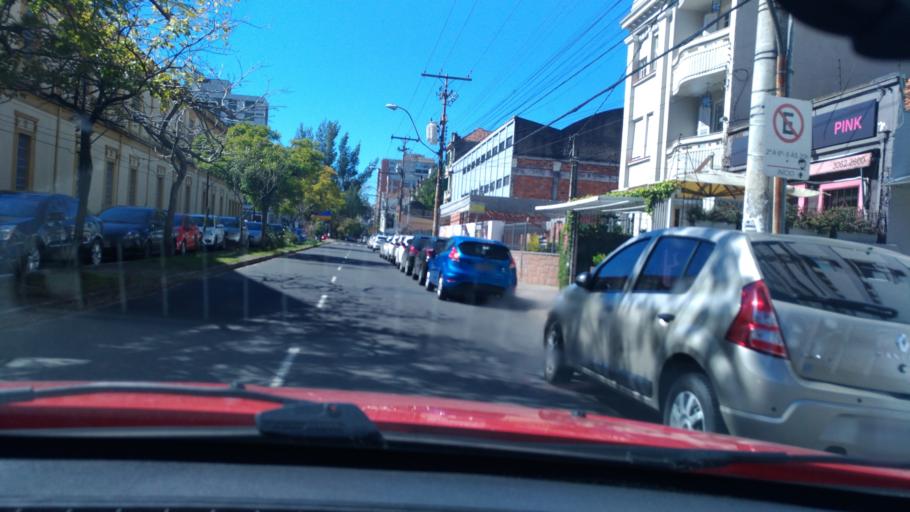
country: BR
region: Rio Grande do Sul
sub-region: Porto Alegre
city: Porto Alegre
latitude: -30.0393
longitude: -51.2131
